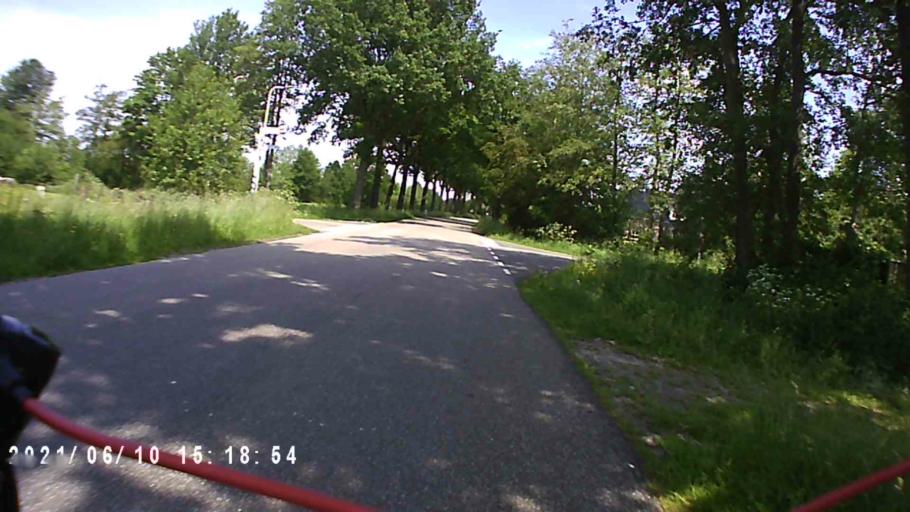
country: NL
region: Friesland
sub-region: Gemeente Achtkarspelen
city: Surhuisterveen
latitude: 53.1963
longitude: 6.1702
